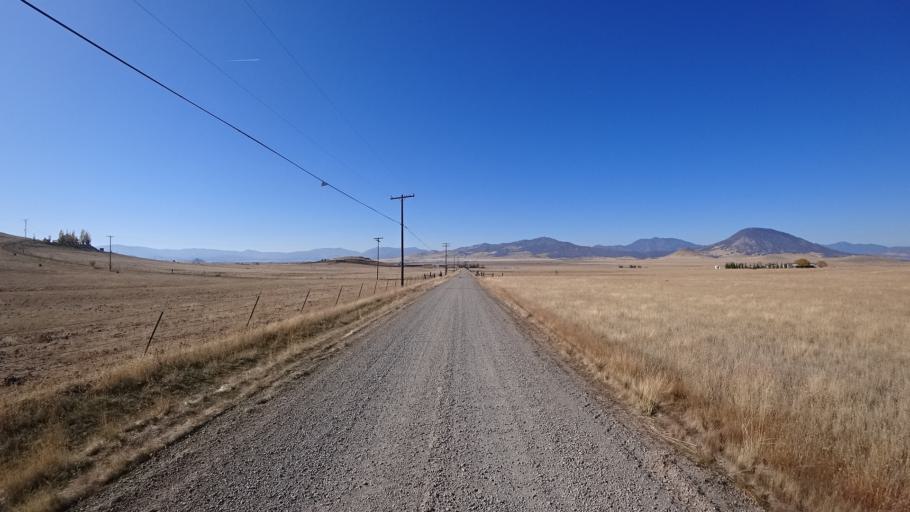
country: US
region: California
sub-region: Siskiyou County
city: Montague
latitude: 41.7939
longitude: -122.4193
